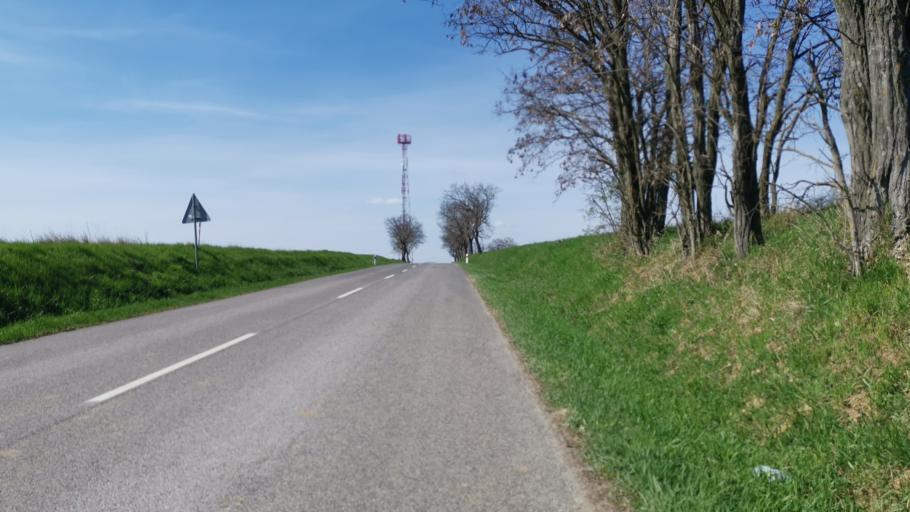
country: SK
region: Trnavsky
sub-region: Okres Skalica
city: Holic
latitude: 48.7411
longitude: 17.2044
